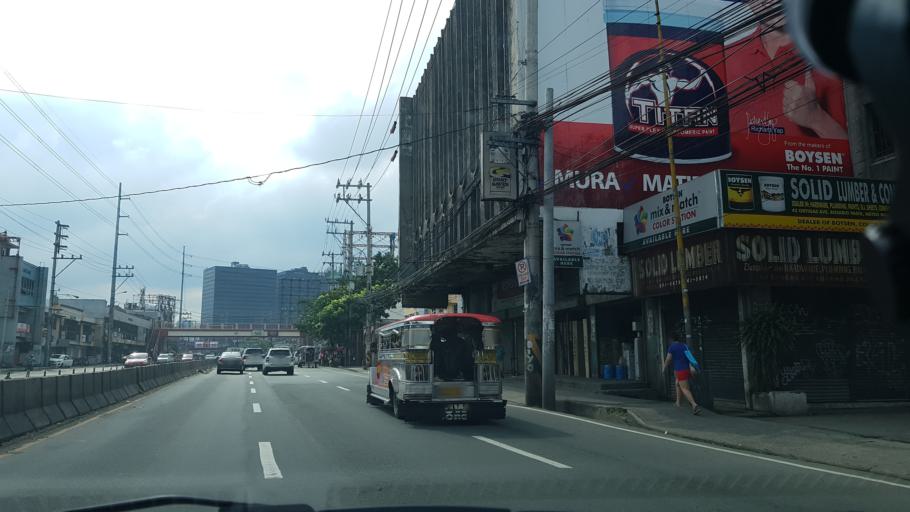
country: PH
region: Metro Manila
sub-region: Pasig
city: Pasig City
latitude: 14.5905
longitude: 121.0882
